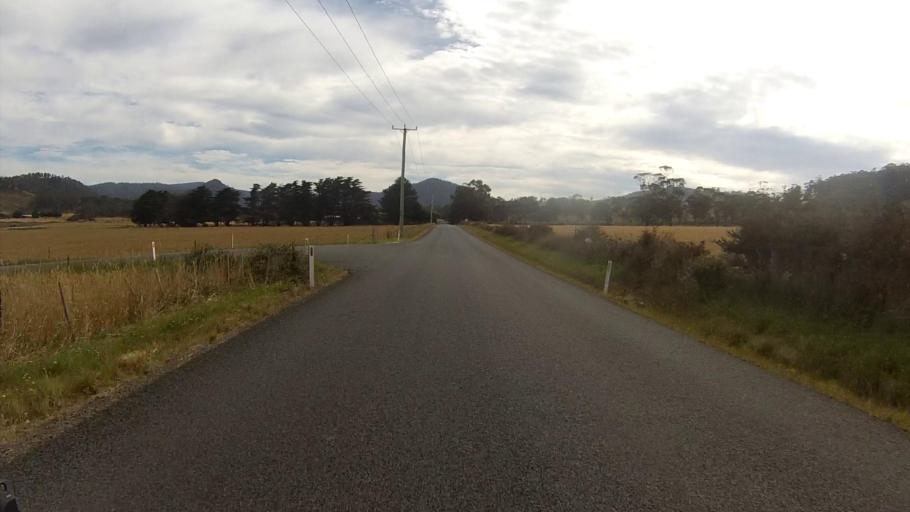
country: AU
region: Tasmania
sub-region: Sorell
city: Sorell
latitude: -42.7951
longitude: 147.7952
